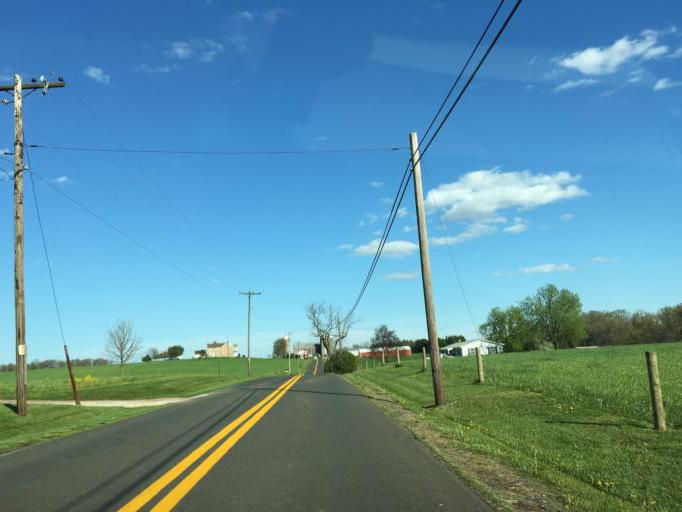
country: US
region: Maryland
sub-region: Frederick County
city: Woodsboro
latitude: 39.6209
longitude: -77.2803
